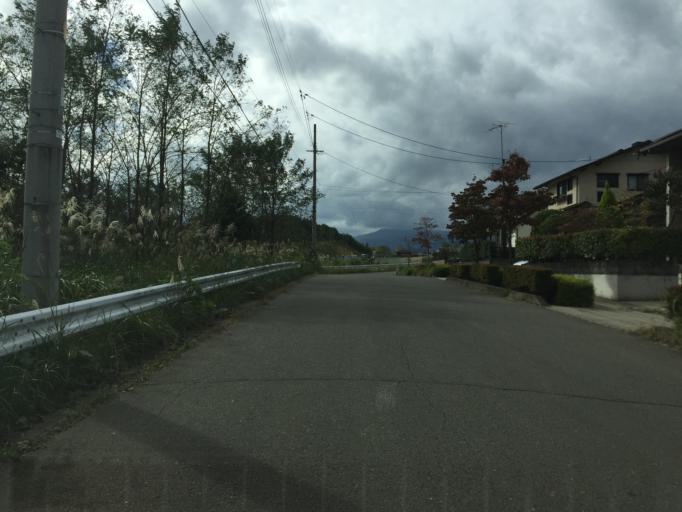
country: JP
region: Fukushima
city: Fukushima-shi
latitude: 37.6938
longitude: 140.4671
